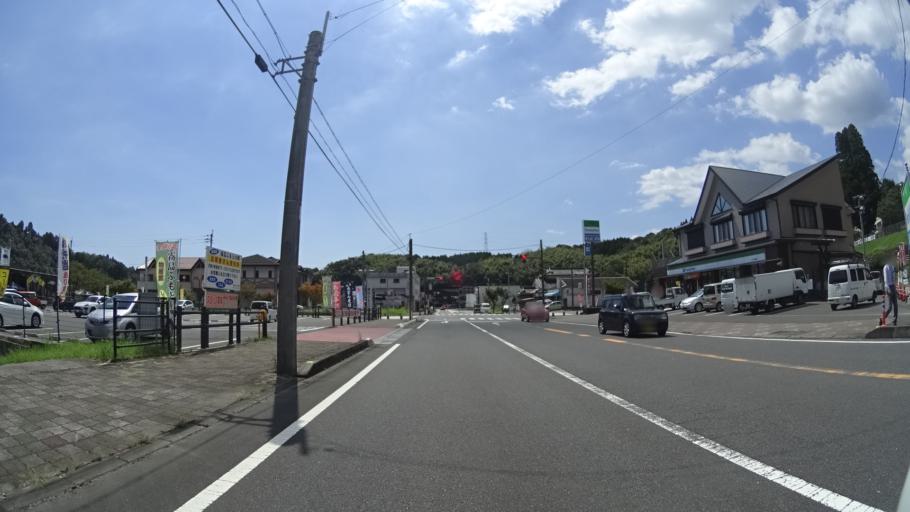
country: JP
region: Kagoshima
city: Kokubu-matsuki
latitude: 31.8559
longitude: 130.7542
